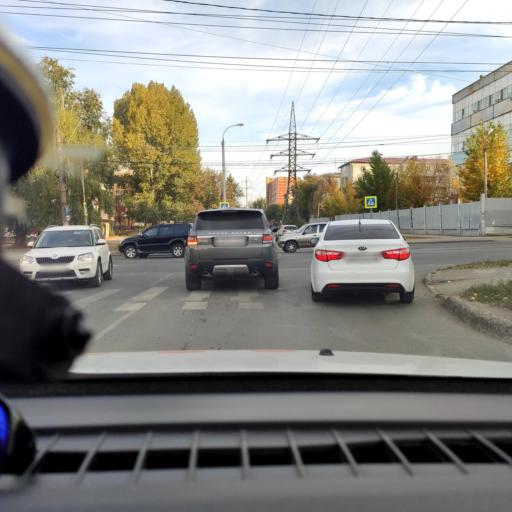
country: RU
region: Samara
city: Samara
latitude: 53.1908
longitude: 50.1720
